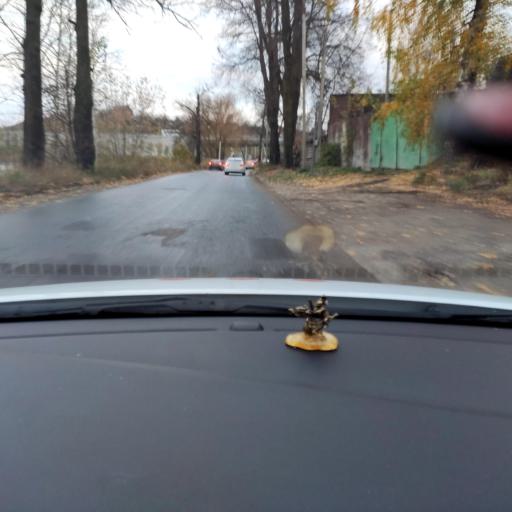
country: RU
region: Tatarstan
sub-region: Gorod Kazan'
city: Kazan
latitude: 55.7283
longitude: 49.1580
